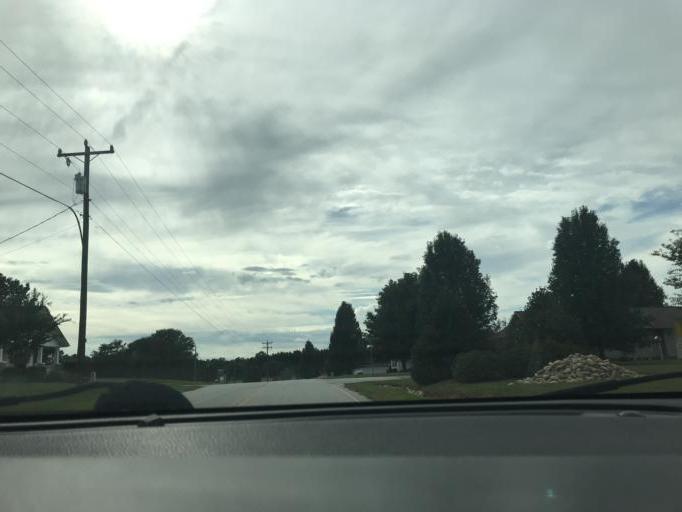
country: US
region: South Carolina
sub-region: Cherokee County
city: Gaffney
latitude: 35.1368
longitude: -81.6849
